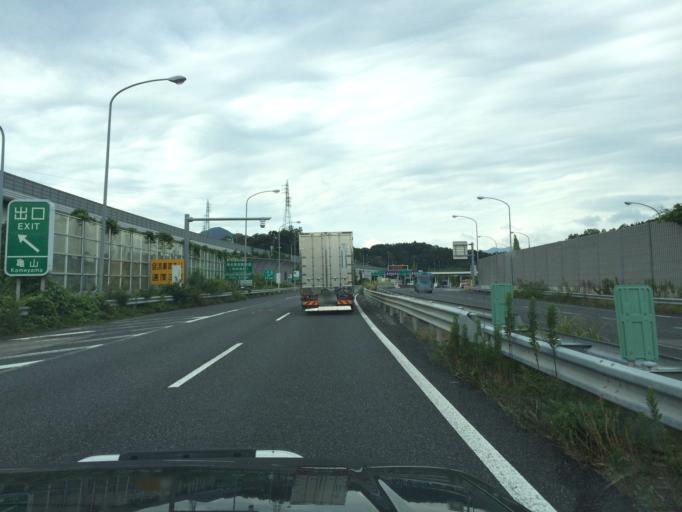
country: JP
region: Mie
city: Kameyama
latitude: 34.8588
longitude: 136.4140
